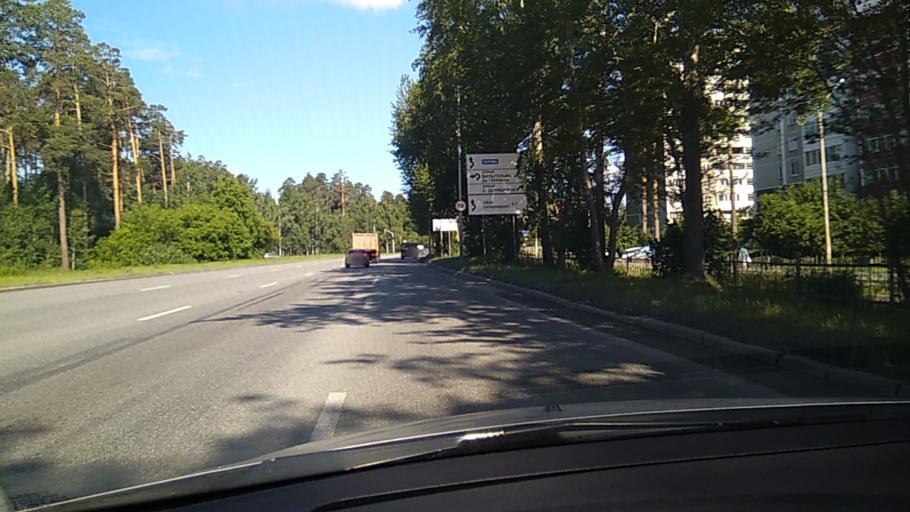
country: RU
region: Sverdlovsk
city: Sovkhoznyy
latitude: 56.8031
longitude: 60.5439
